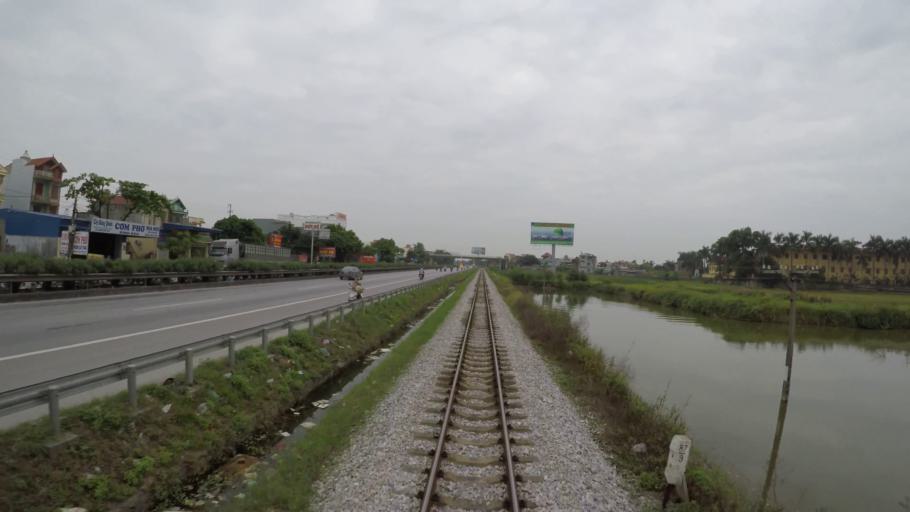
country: VN
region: Hai Duong
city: Phu Thai
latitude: 20.9231
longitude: 106.5587
